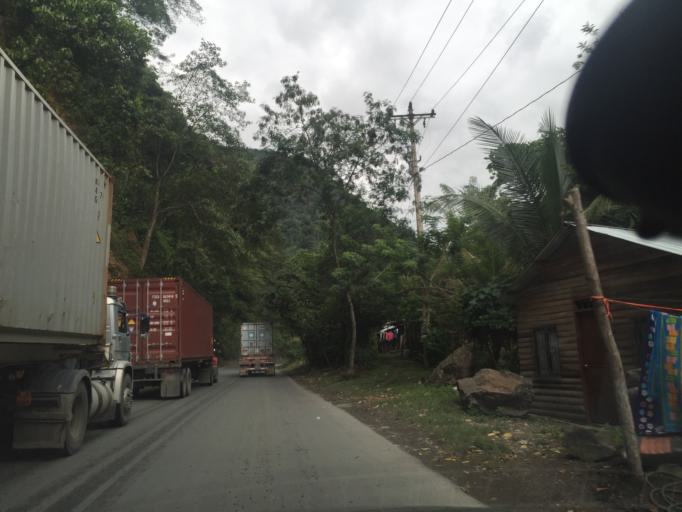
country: CO
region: Valle del Cauca
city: Dagua
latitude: 3.7766
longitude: -76.7512
